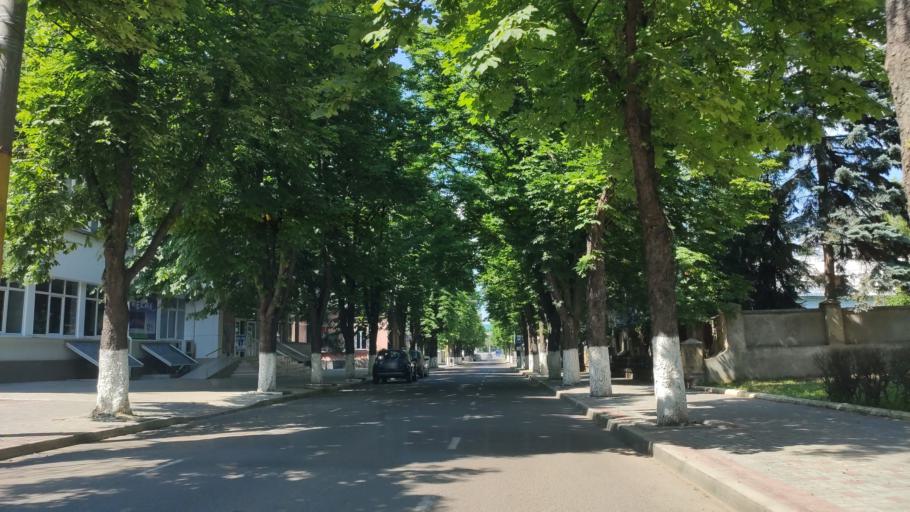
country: MD
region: Raionul Soroca
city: Soroca
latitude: 48.1543
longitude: 28.3021
